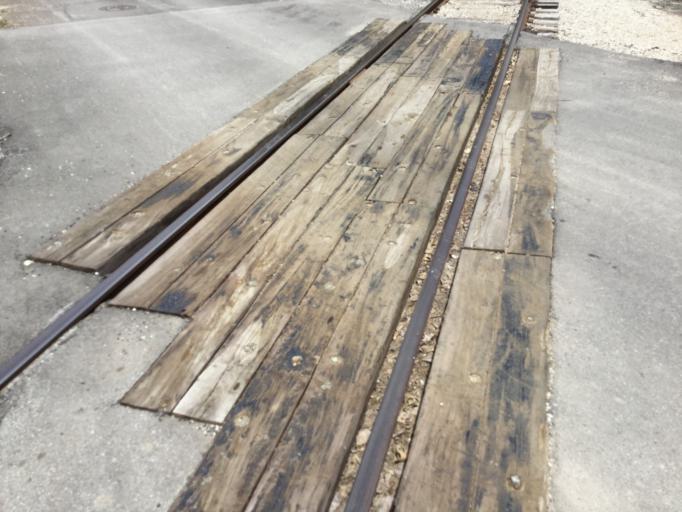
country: US
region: Kansas
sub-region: Johnson County
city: De Soto
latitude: 38.9795
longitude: -94.9733
